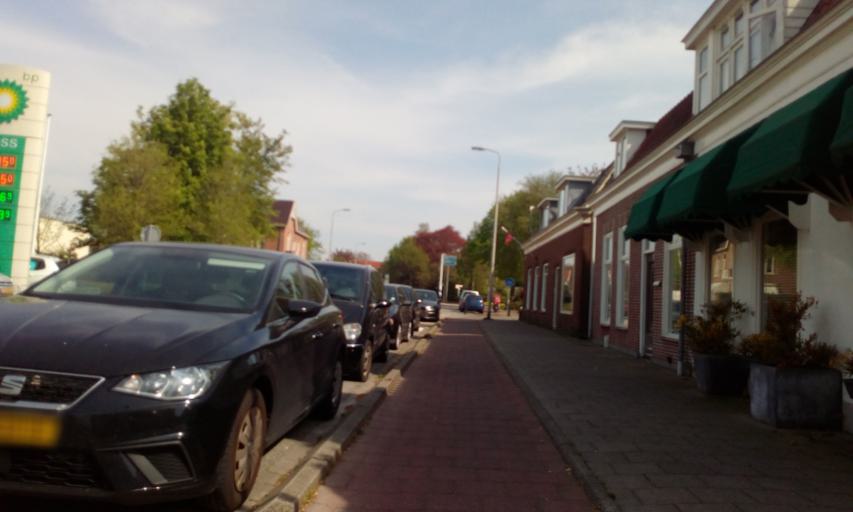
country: NL
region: South Holland
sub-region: Gemeente Lisse
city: Lisse
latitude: 52.2654
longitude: 4.5583
